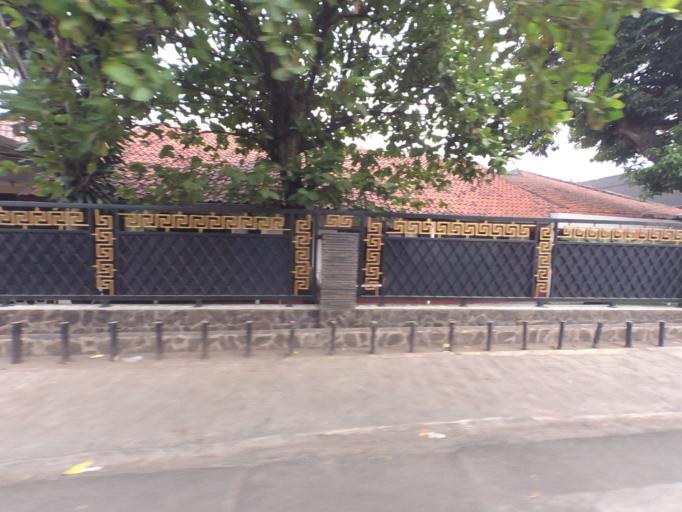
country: ID
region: West Java
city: Ciampea
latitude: -6.5573
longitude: 106.6932
